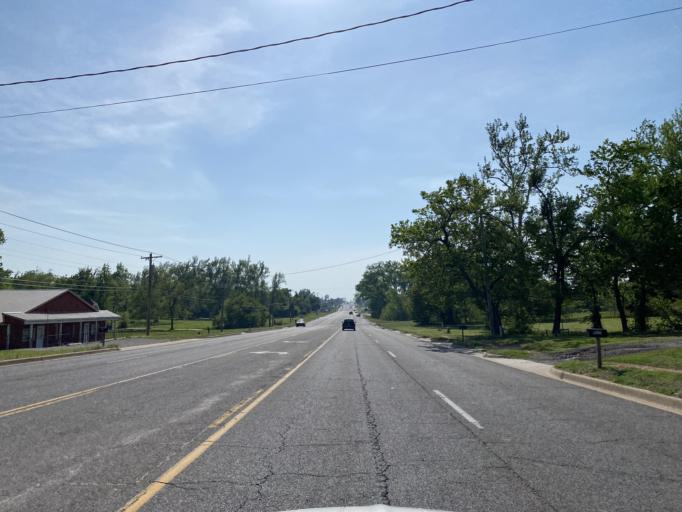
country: US
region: Oklahoma
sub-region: Oklahoma County
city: Spencer
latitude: 35.4931
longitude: -97.3602
